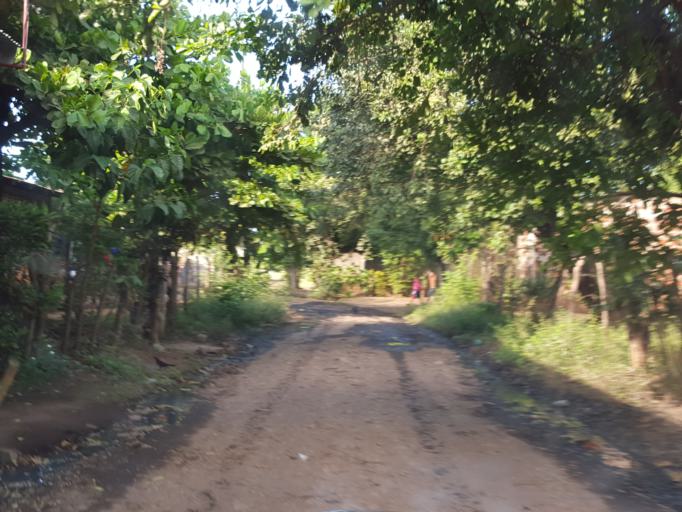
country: NI
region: Leon
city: Leon
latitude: 12.4242
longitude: -86.9084
